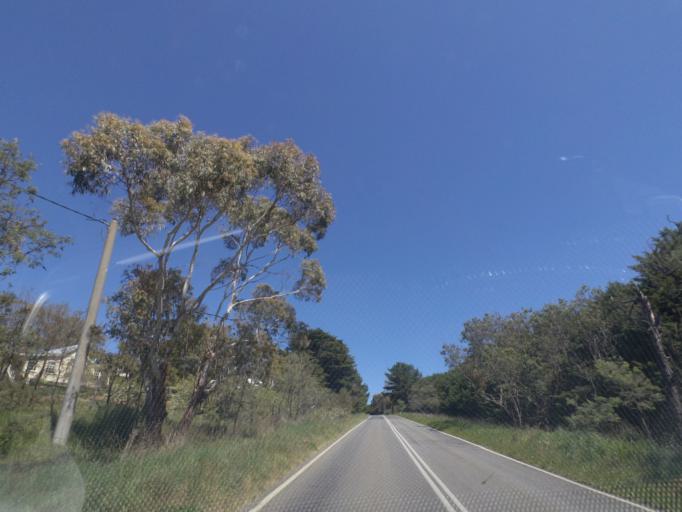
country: AU
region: Victoria
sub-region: Hume
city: Sunbury
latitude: -37.3028
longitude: 144.6855
